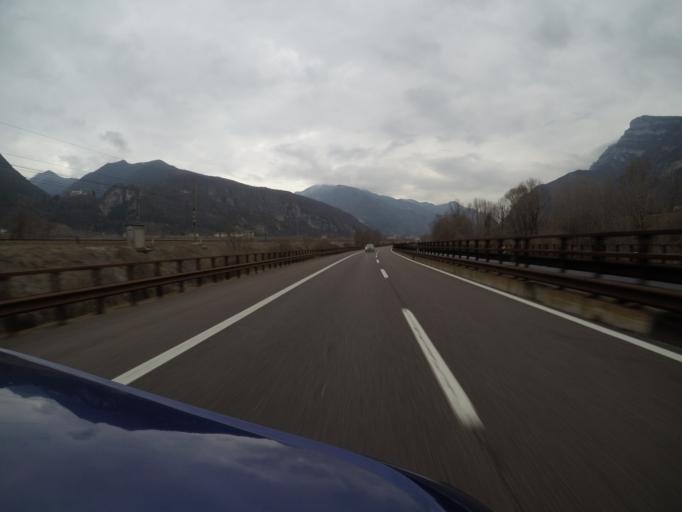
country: IT
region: Trentino-Alto Adige
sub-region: Provincia di Trento
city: Ala
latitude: 45.7893
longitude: 11.0200
